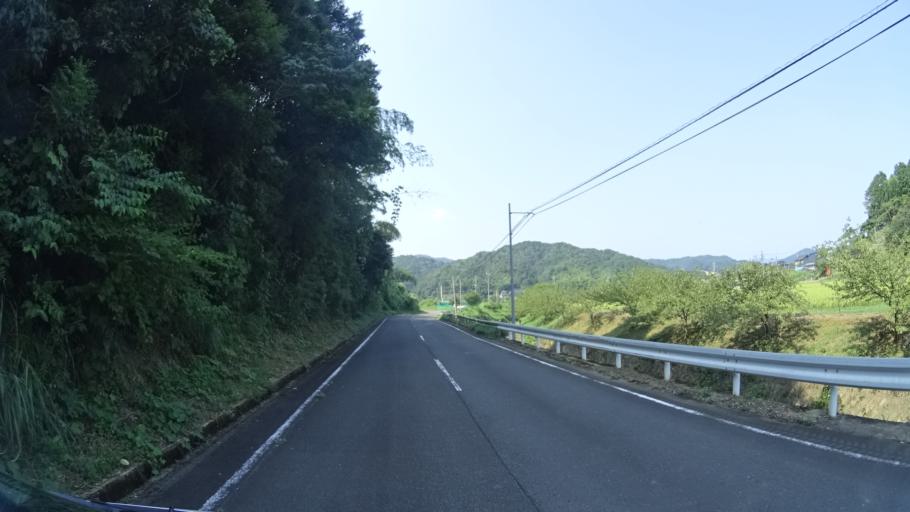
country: JP
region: Kyoto
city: Ayabe
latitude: 35.4069
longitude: 135.1971
